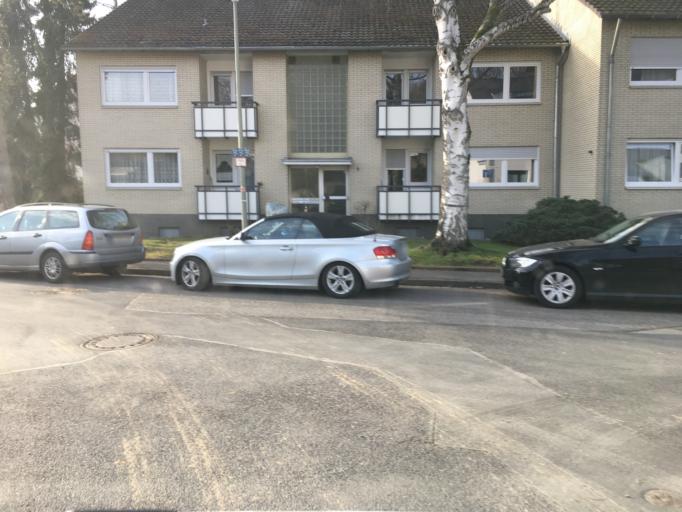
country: DE
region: North Rhine-Westphalia
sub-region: Regierungsbezirk Koln
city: Rosrath
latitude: 50.9193
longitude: 7.1763
